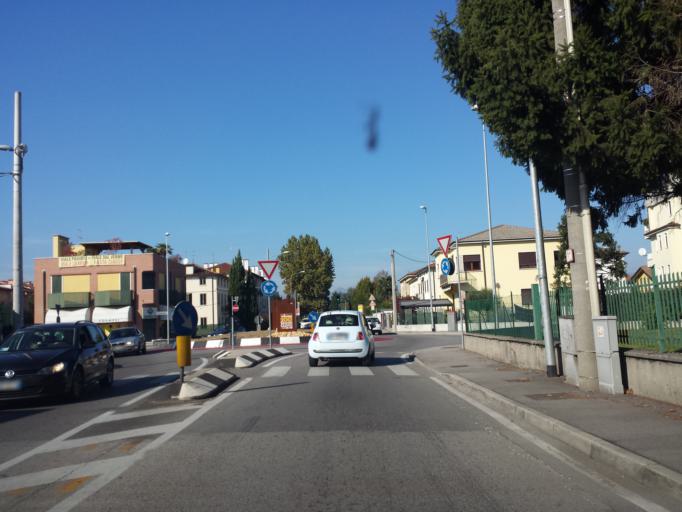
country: IT
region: Veneto
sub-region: Provincia di Vicenza
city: Crispi Cavour
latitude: 45.5702
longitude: 11.5147
